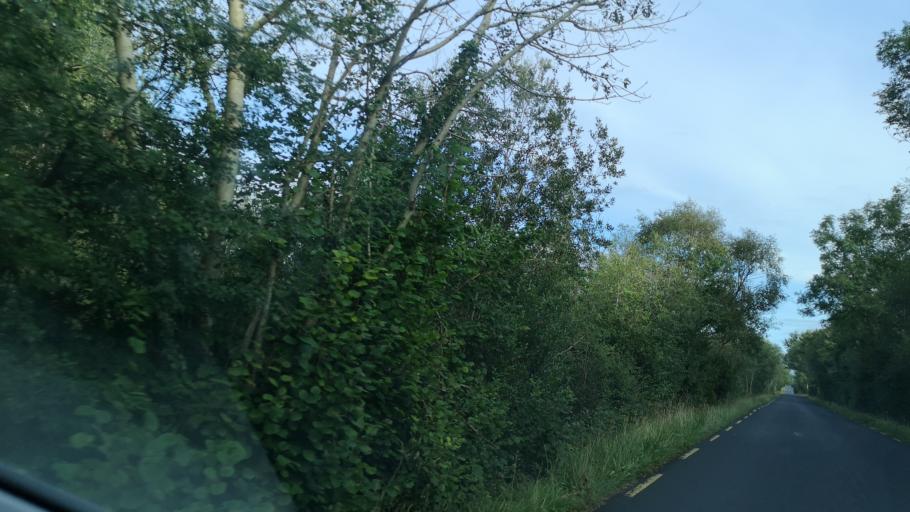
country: IE
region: Connaught
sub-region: County Galway
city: Ballinasloe
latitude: 53.3364
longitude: -8.2871
